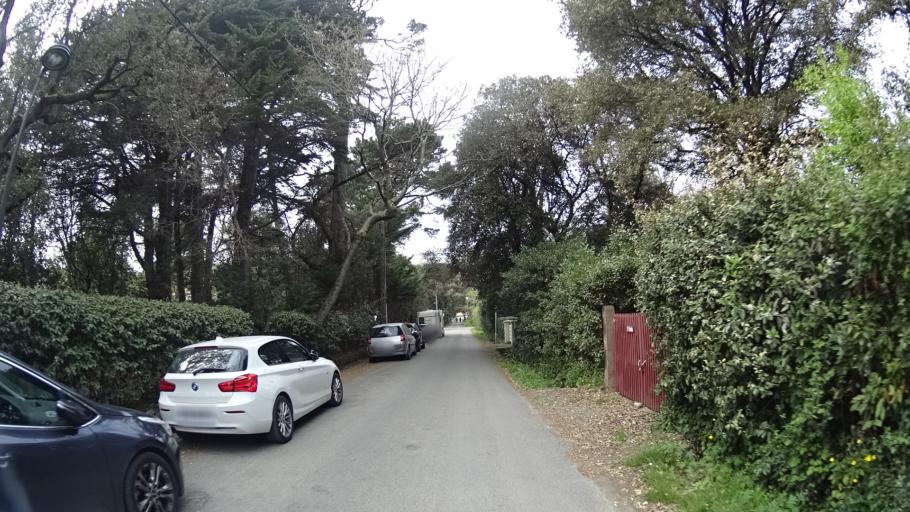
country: FR
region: Pays de la Loire
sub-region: Departement de la Vendee
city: La Gueriniere
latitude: 47.0114
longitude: -2.2269
